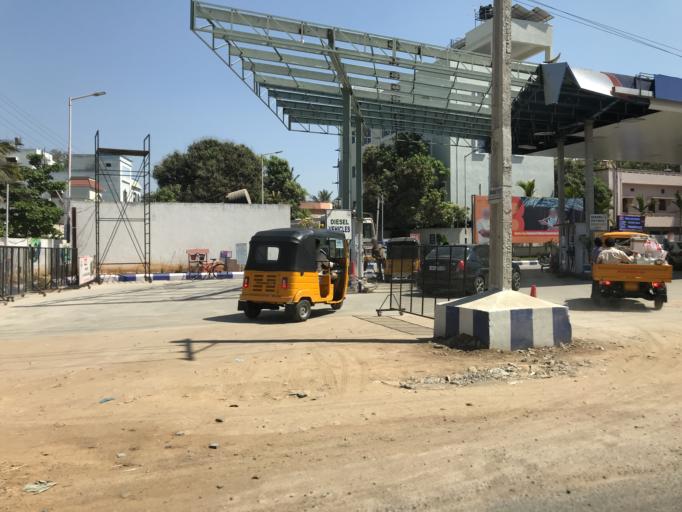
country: IN
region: Telangana
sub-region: Medak
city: Serilingampalle
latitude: 17.4734
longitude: 78.3270
